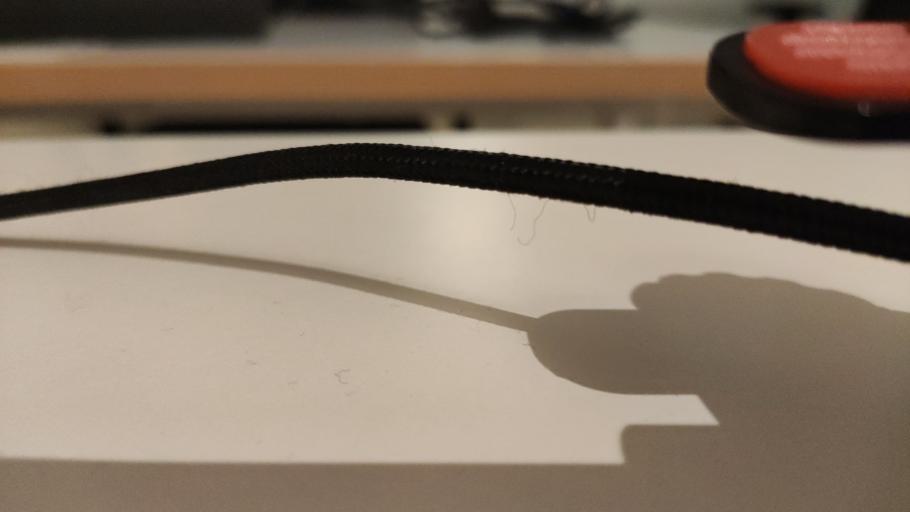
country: RU
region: Moskovskaya
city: Kurovskoye
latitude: 55.5757
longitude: 38.8876
